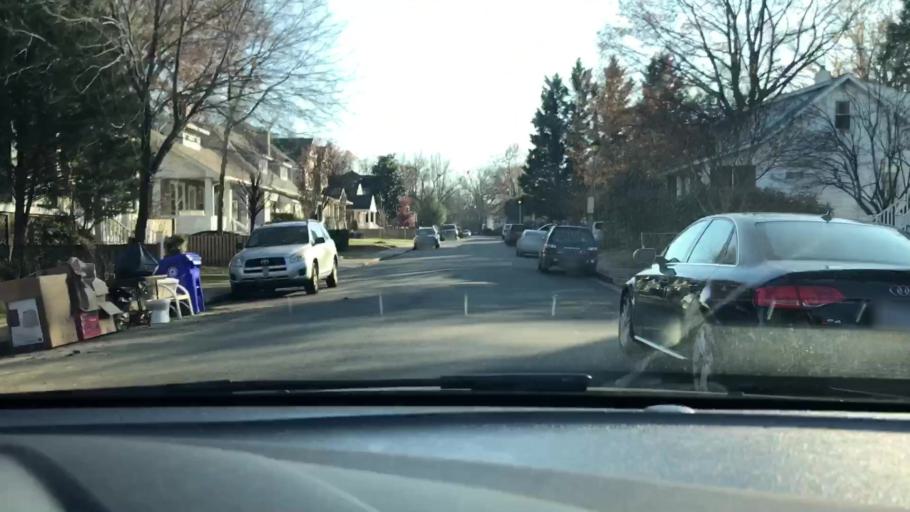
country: US
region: Virginia
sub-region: Arlington County
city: Arlington
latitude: 38.8820
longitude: -77.0999
